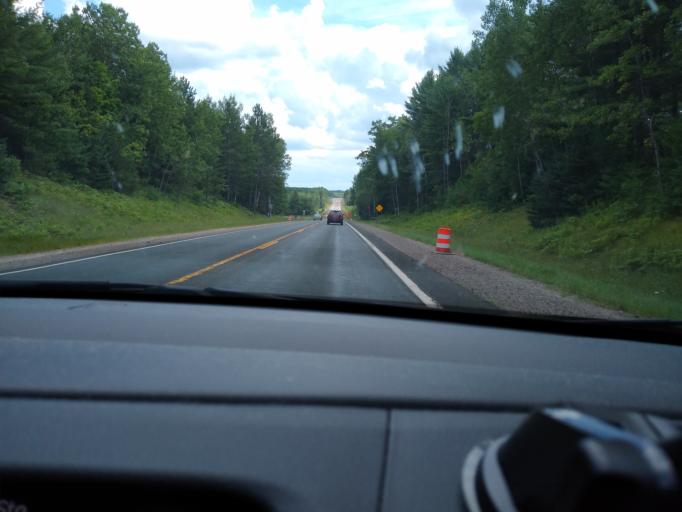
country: US
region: Michigan
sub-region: Iron County
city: Crystal Falls
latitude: 46.2514
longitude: -88.0113
